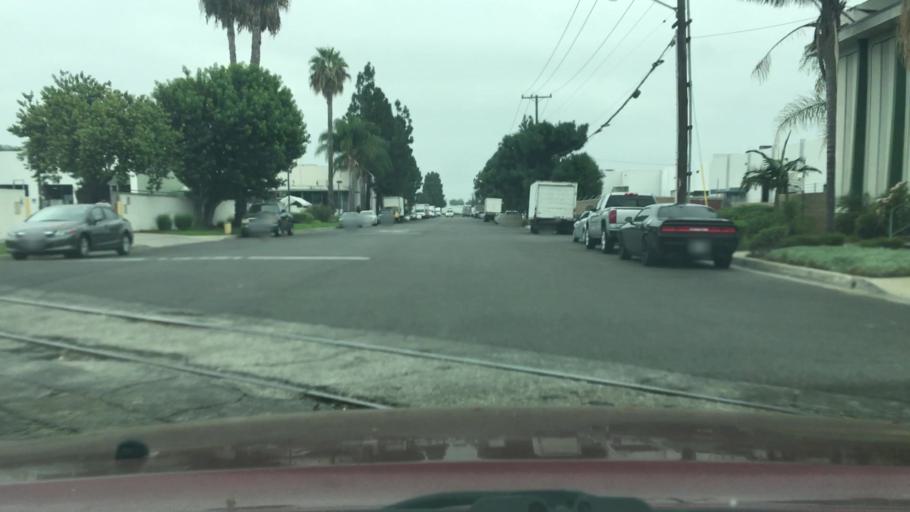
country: US
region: California
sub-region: Orange County
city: Buena Park
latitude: 33.8860
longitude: -118.0216
